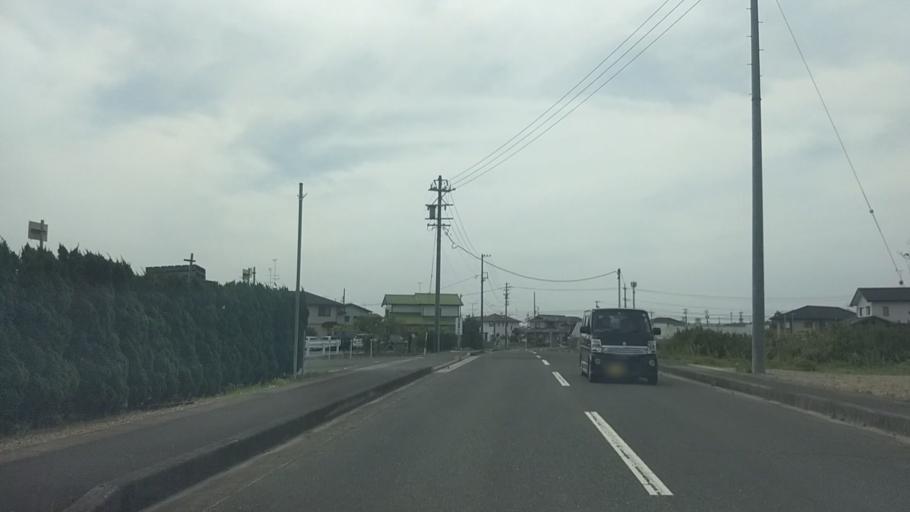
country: JP
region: Shizuoka
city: Kosai-shi
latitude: 34.7312
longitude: 137.5256
